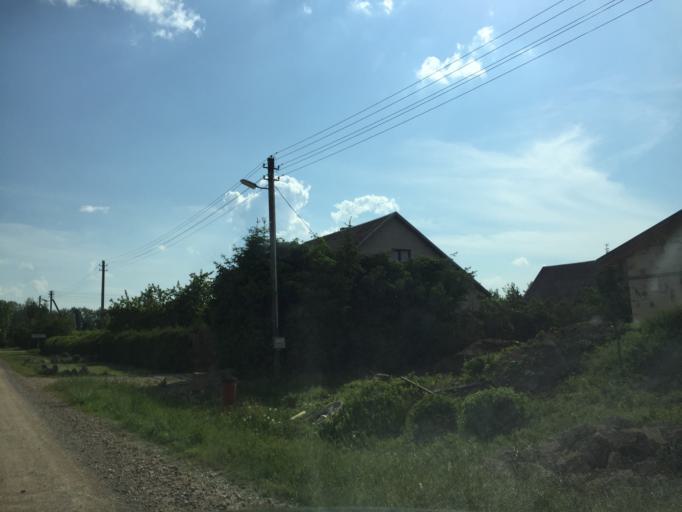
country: LT
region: Klaipedos apskritis
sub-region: Klaipeda
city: Palanga
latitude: 55.9048
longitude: 21.1338
